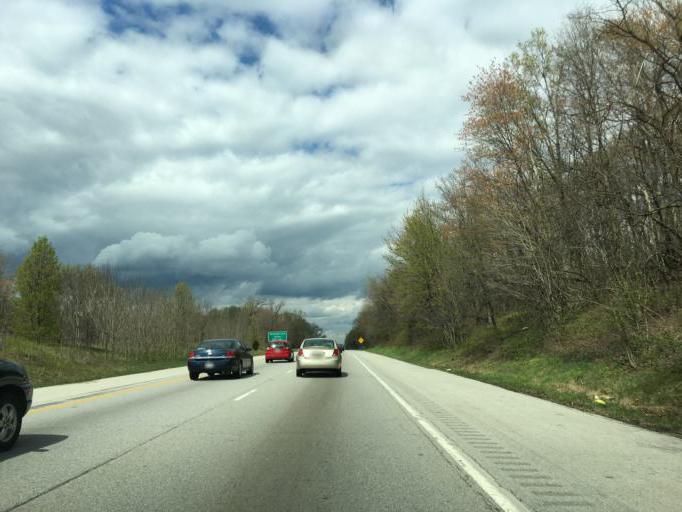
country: US
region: Maryland
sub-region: Anne Arundel County
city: Jessup
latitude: 39.1408
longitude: -76.7551
